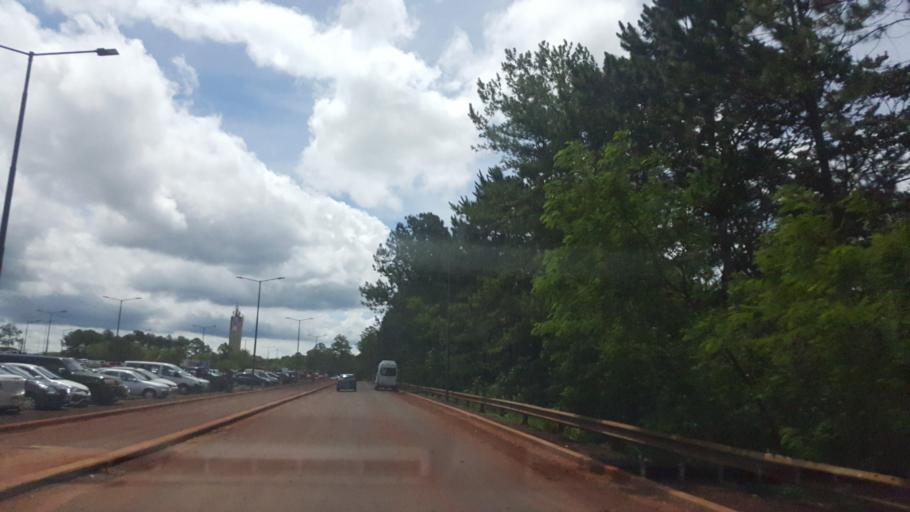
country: AR
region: Misiones
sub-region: Departamento de Iguazu
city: Puerto Iguazu
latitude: -25.7309
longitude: -54.4750
